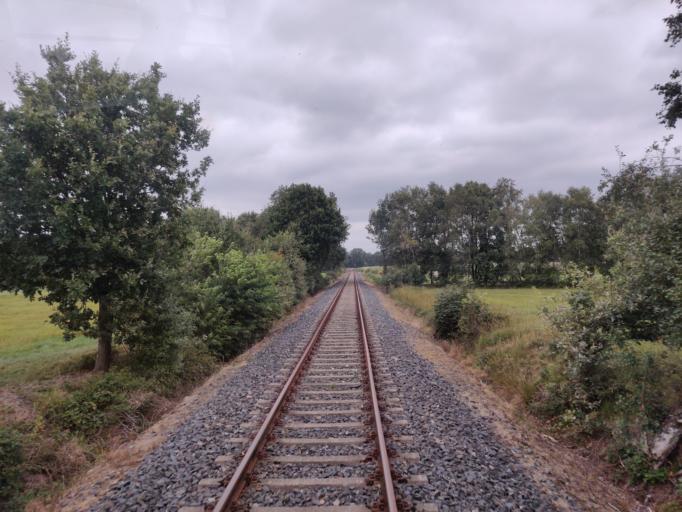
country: DE
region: Lower Saxony
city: Vollersode
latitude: 53.2887
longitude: 8.9698
